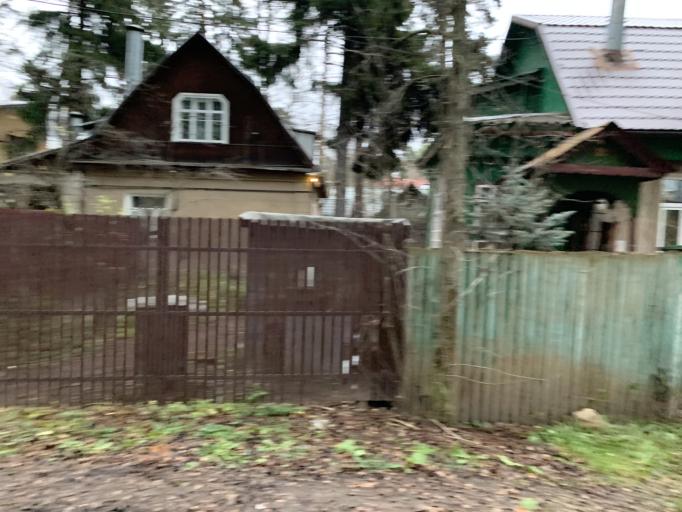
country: RU
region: Moskovskaya
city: Mamontovka
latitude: 55.9851
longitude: 37.8130
